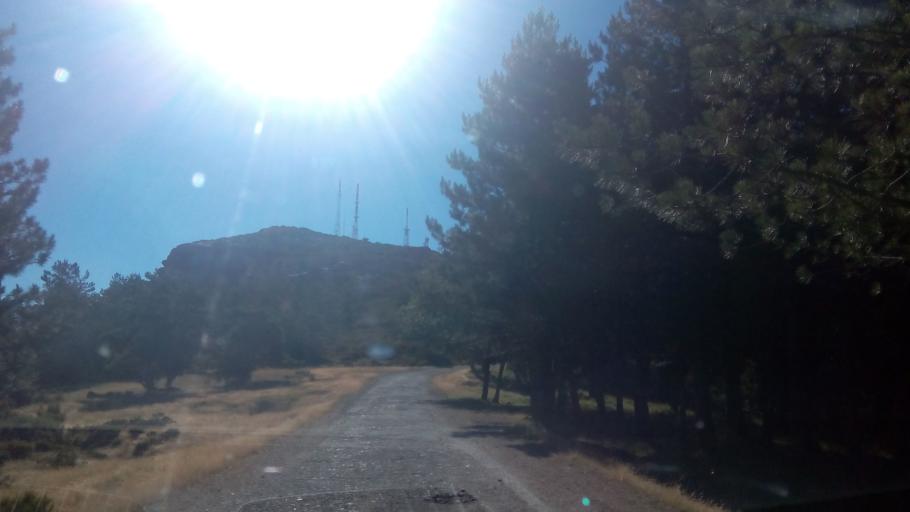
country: PT
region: Vila Real
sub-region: Mesao Frio
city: Mesao Frio
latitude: 41.2486
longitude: -7.8937
